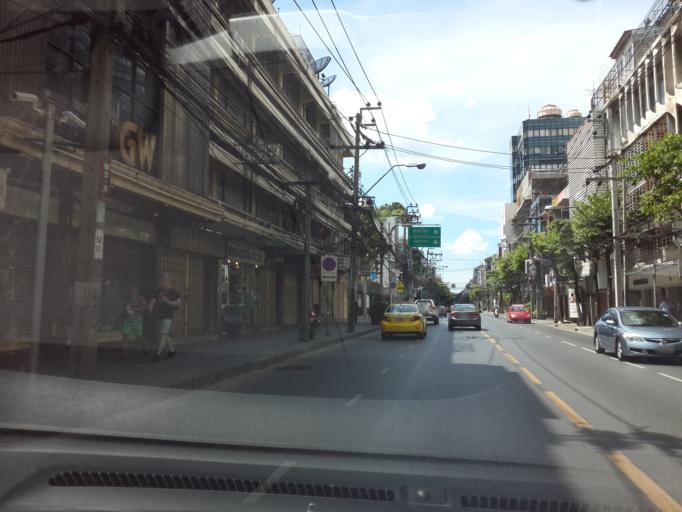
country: TH
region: Bangkok
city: Samphanthawong
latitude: 13.7226
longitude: 100.5167
